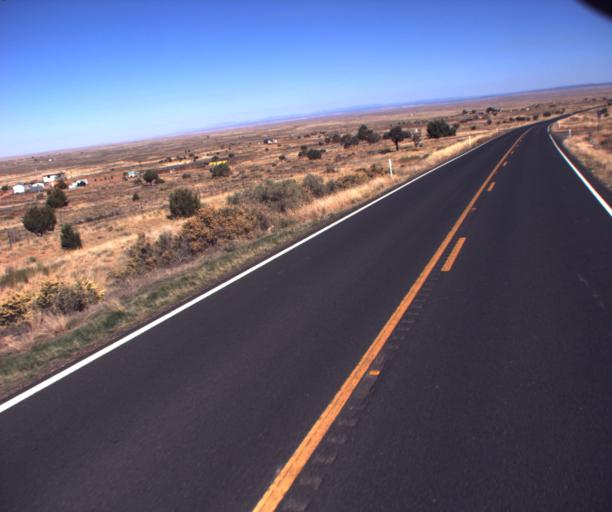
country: US
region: Arizona
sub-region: Apache County
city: Ganado
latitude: 35.7780
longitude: -109.7297
